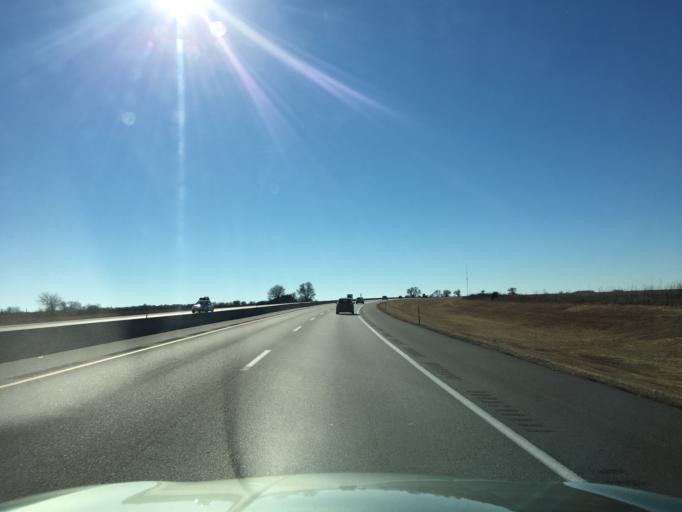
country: US
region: Kansas
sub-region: Sumner County
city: Belle Plaine
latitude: 37.3472
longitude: -97.3221
